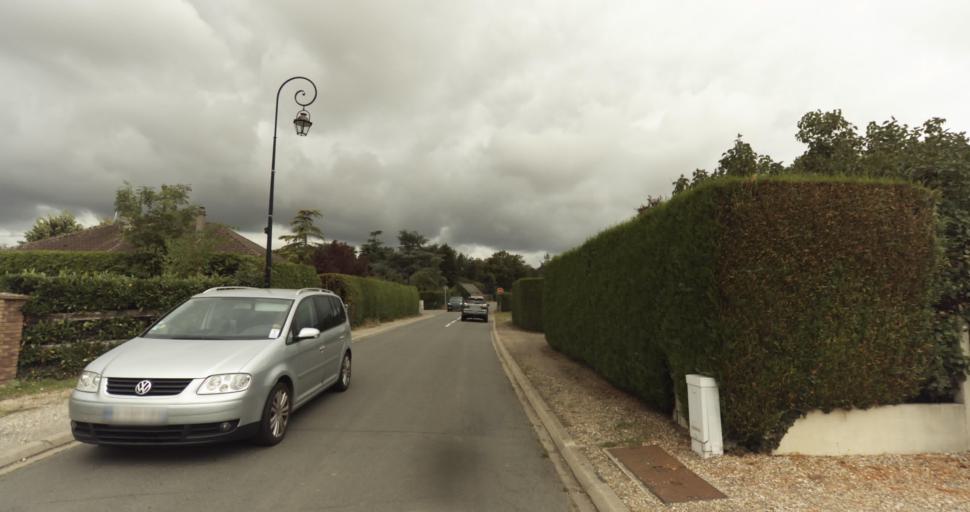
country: FR
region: Haute-Normandie
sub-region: Departement de l'Eure
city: Gravigny
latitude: 48.9900
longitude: 1.2466
